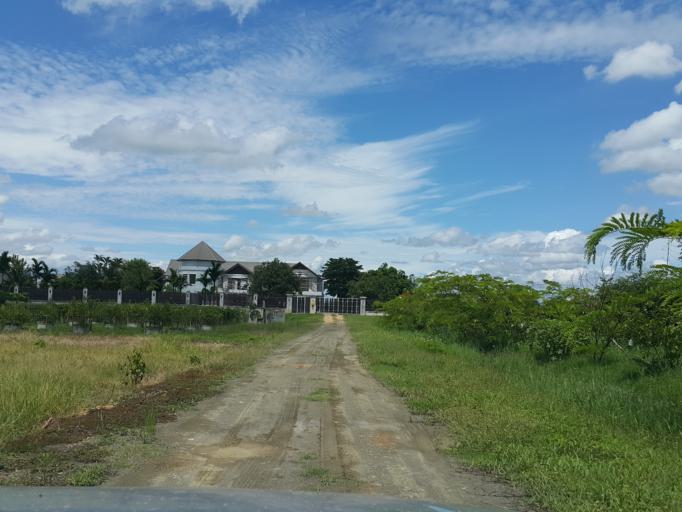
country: TH
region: Chiang Mai
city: San Kamphaeng
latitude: 18.7688
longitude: 99.1035
